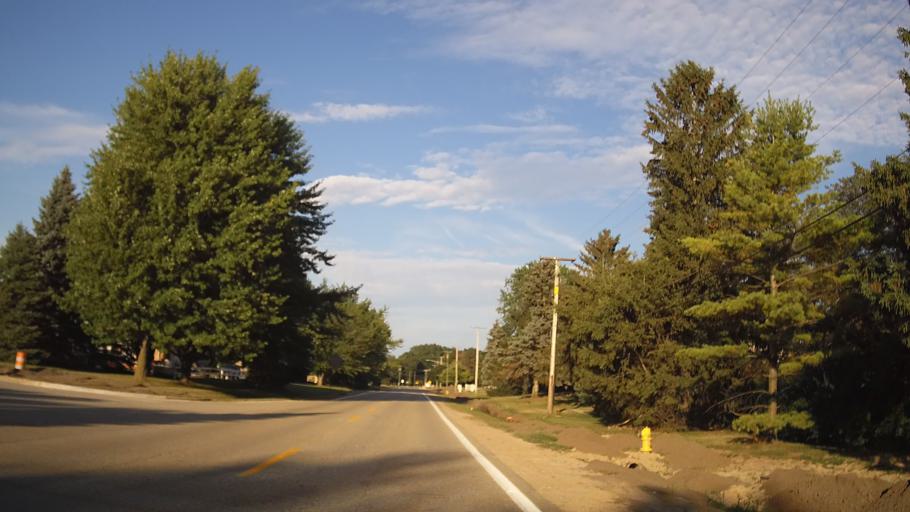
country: US
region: Michigan
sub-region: Macomb County
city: Clinton
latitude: 42.5838
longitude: -82.9476
